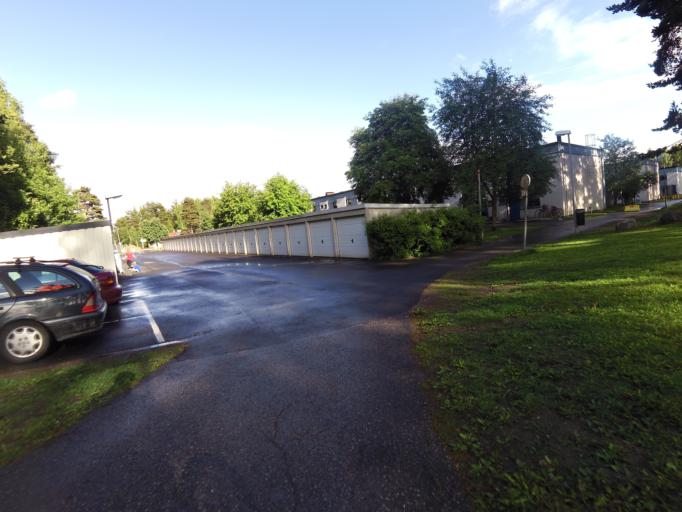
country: SE
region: Gaevleborg
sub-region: Gavle Kommun
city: Gavle
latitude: 60.6919
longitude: 17.1022
